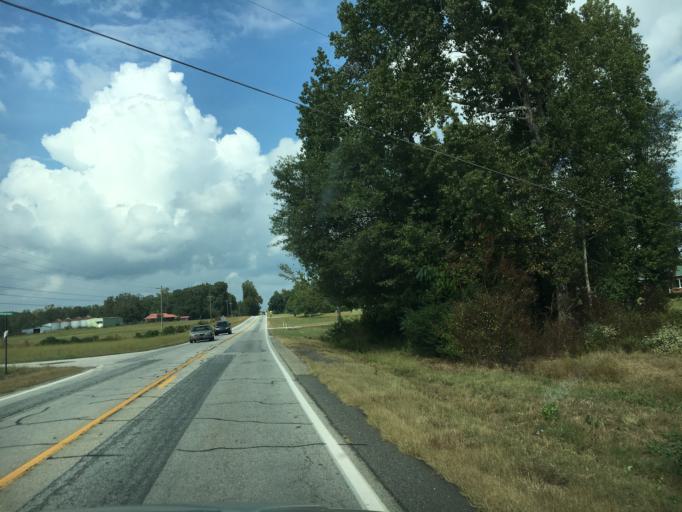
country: US
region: Georgia
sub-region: Elbert County
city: Elberton
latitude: 34.1859
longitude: -82.8895
